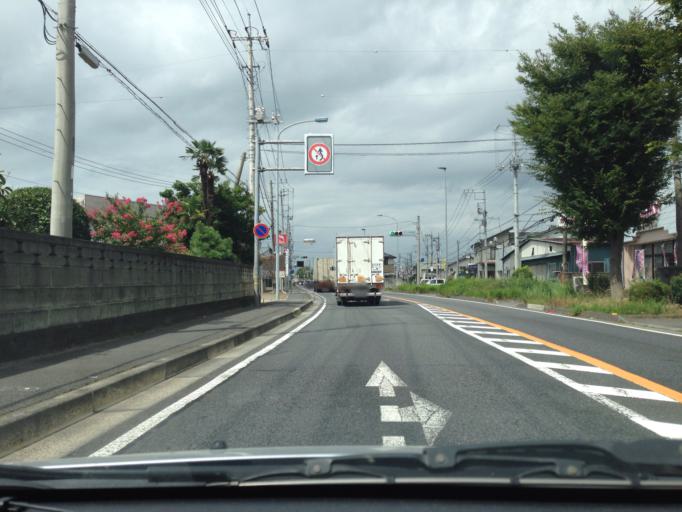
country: JP
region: Ibaraki
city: Naka
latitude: 36.0243
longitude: 140.1607
